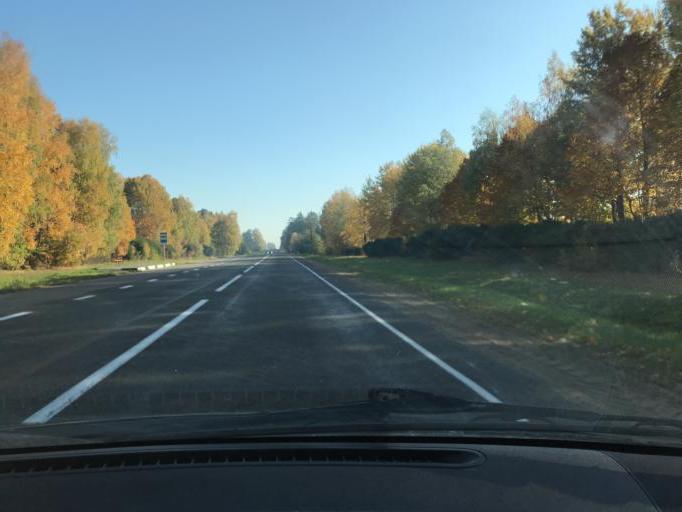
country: BY
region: Brest
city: Lyakhavichy
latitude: 52.9548
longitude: 26.2682
